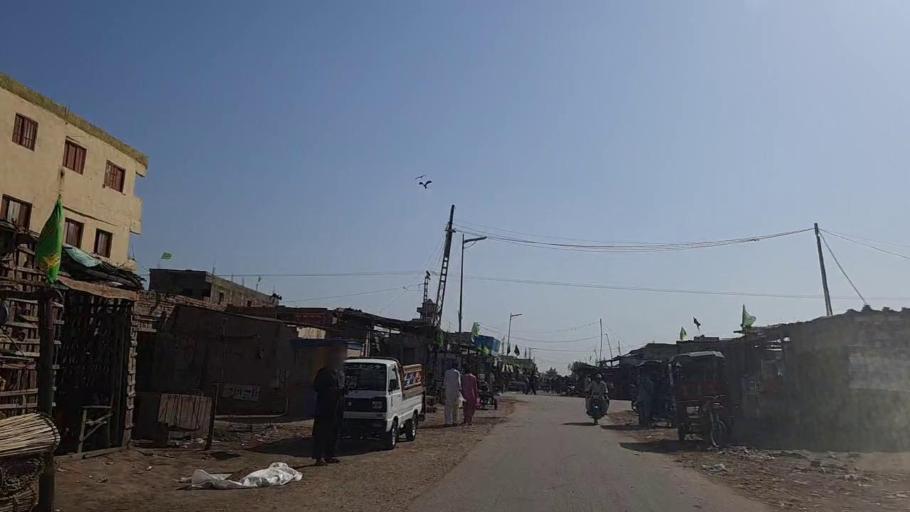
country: PK
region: Sindh
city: Mirpur Batoro
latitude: 24.6186
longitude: 68.2953
